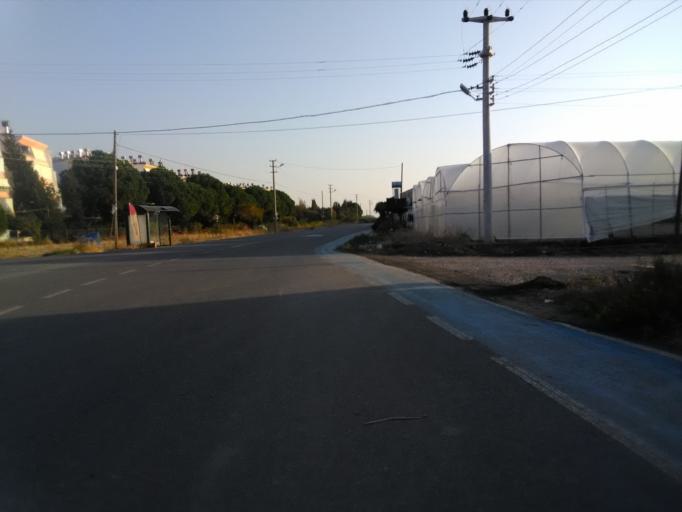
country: TR
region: Antalya
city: Gazipasa
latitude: 36.2566
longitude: 32.2907
